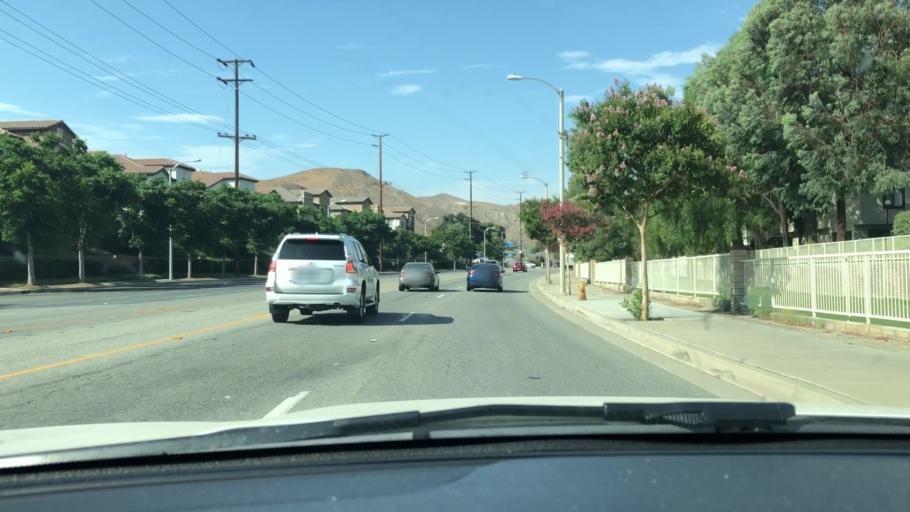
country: US
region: California
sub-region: Los Angeles County
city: Santa Clarita
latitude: 34.4210
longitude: -118.4533
